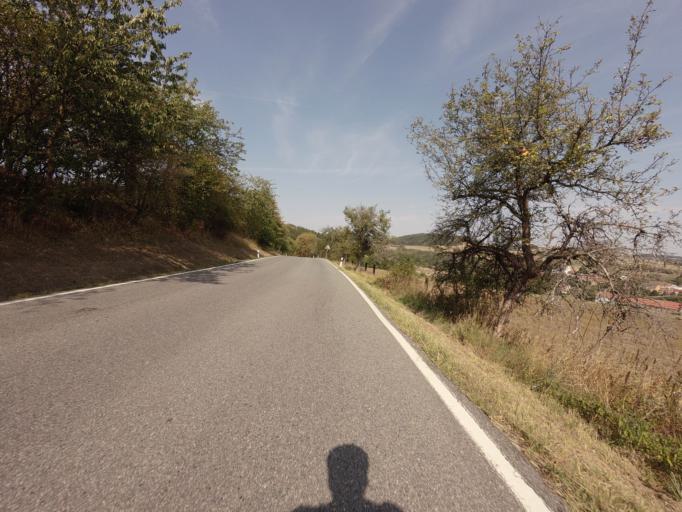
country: CZ
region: Central Bohemia
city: Petrovice
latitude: 49.5906
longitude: 14.3816
